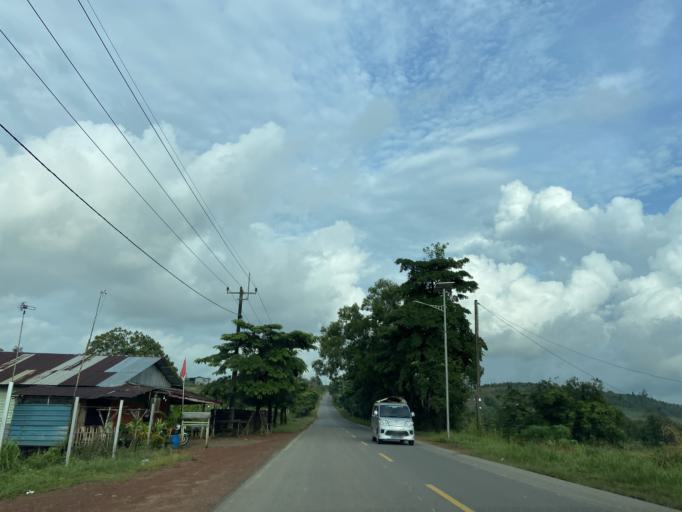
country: ID
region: Riau Islands
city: Tanjungpinang
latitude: 0.9360
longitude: 104.1015
